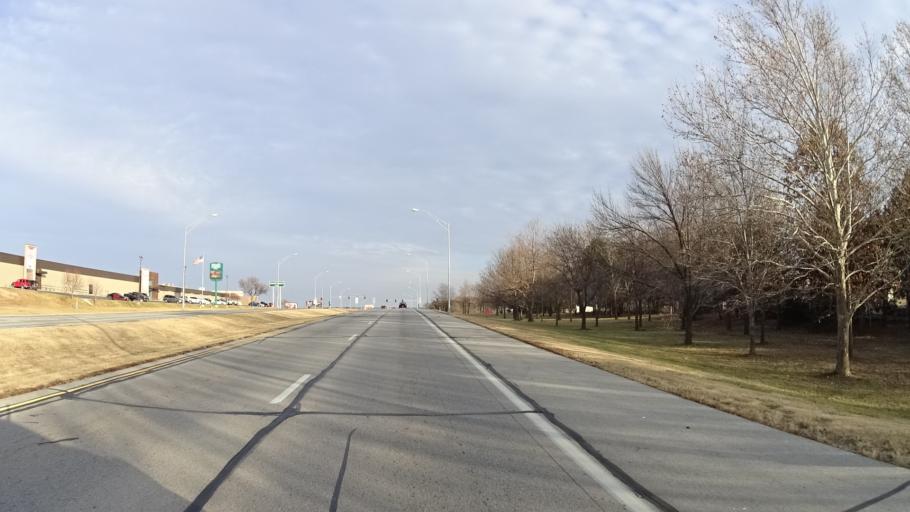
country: US
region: Nebraska
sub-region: Douglas County
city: Ralston
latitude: 41.2124
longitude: -96.0559
